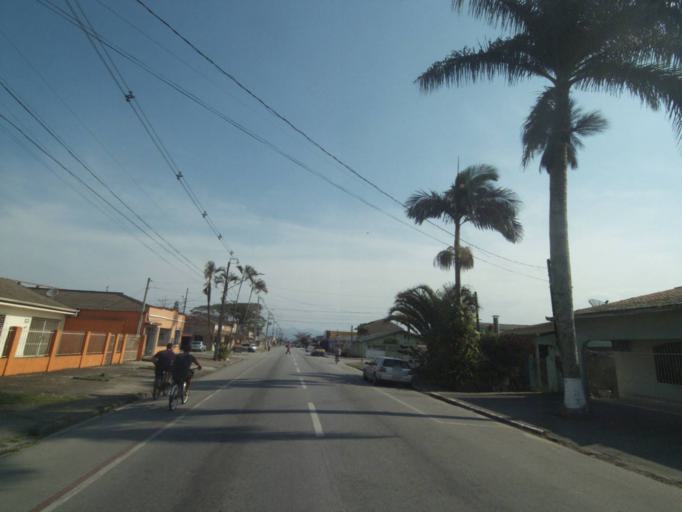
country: BR
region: Parana
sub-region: Paranagua
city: Paranagua
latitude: -25.5262
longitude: -48.5186
